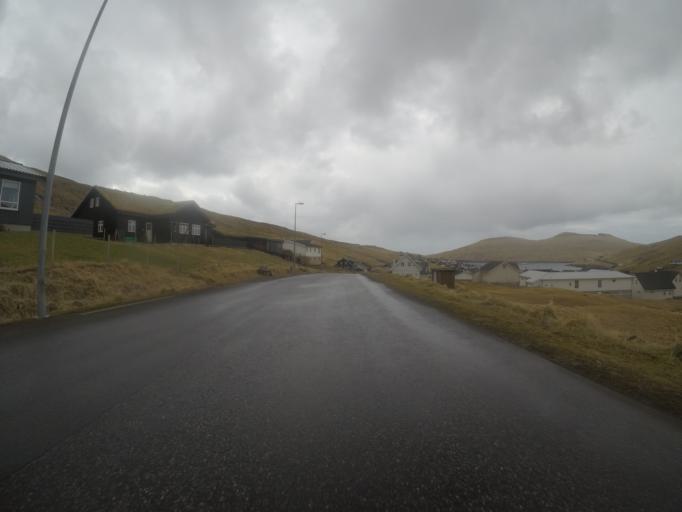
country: FO
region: Vagar
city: Midvagur
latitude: 62.0613
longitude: -7.1452
